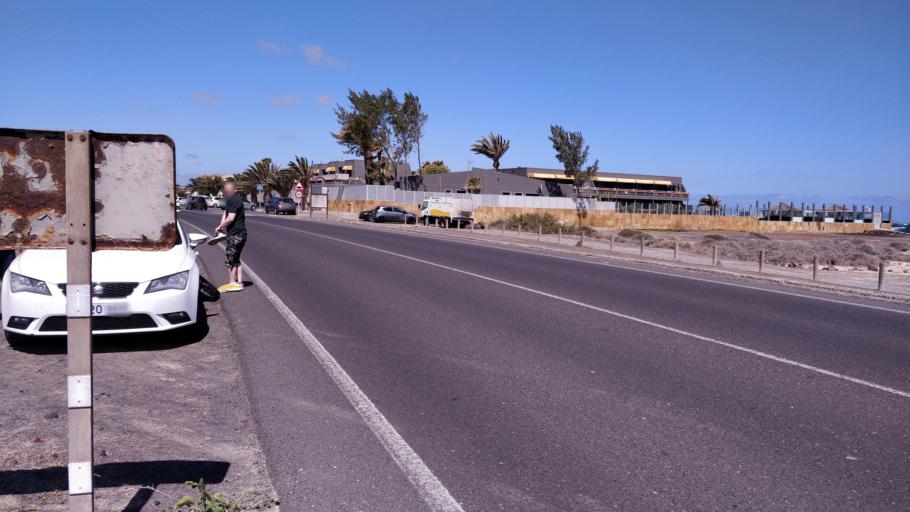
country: ES
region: Canary Islands
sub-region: Provincia de Las Palmas
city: Corralejo
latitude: 28.7258
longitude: -13.8488
